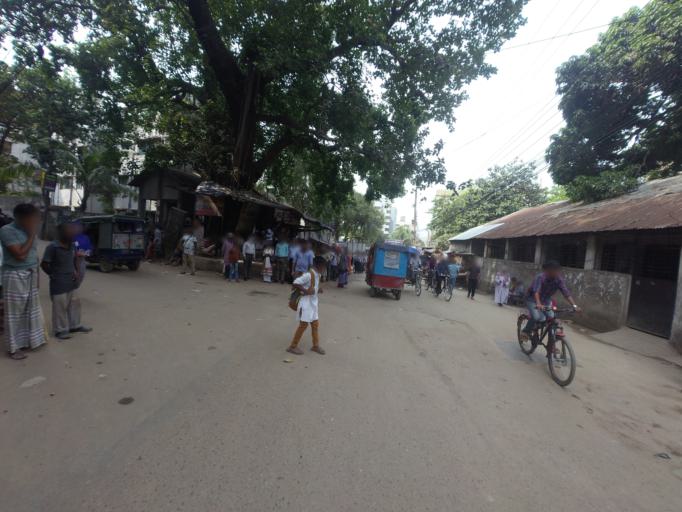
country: BD
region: Dhaka
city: Azimpur
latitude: 23.7245
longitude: 90.3757
